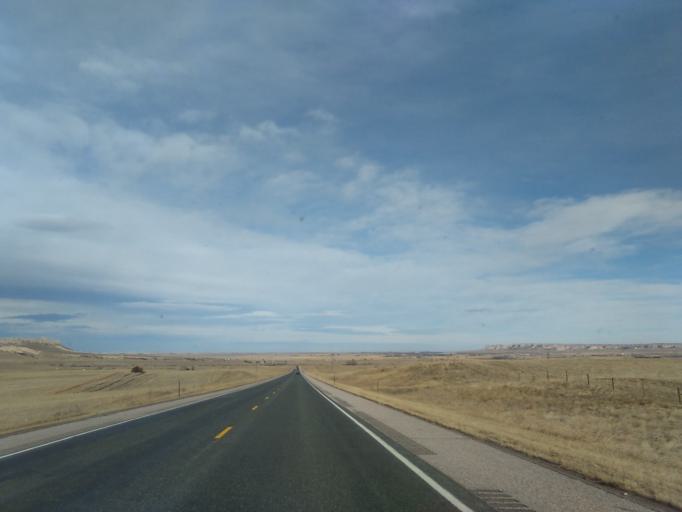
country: US
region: Wyoming
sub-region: Goshen County
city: Torrington
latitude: 41.6165
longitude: -104.2511
